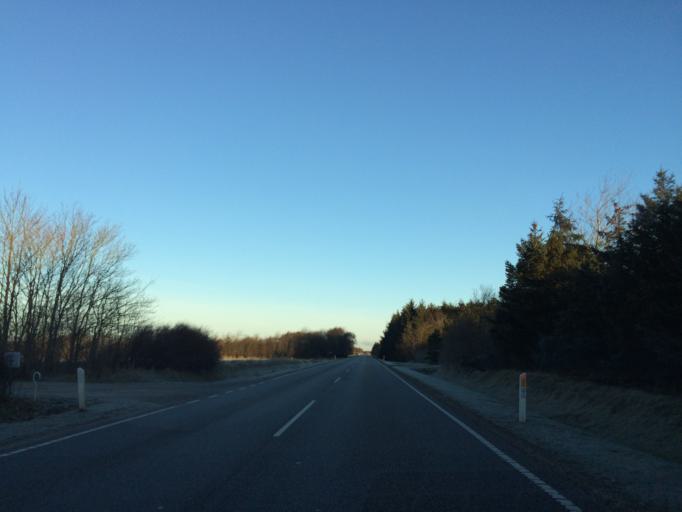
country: DK
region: Central Jutland
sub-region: Holstebro Kommune
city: Ulfborg
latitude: 56.3938
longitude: 8.3206
